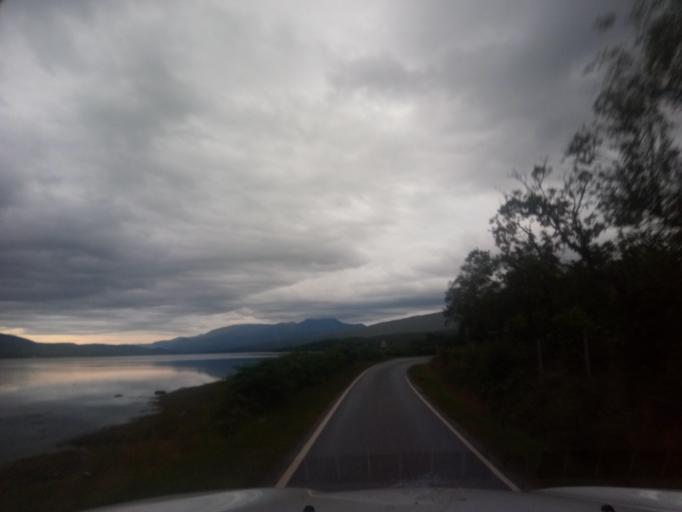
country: GB
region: Scotland
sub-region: Highland
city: Fort William
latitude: 56.8515
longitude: -5.3261
